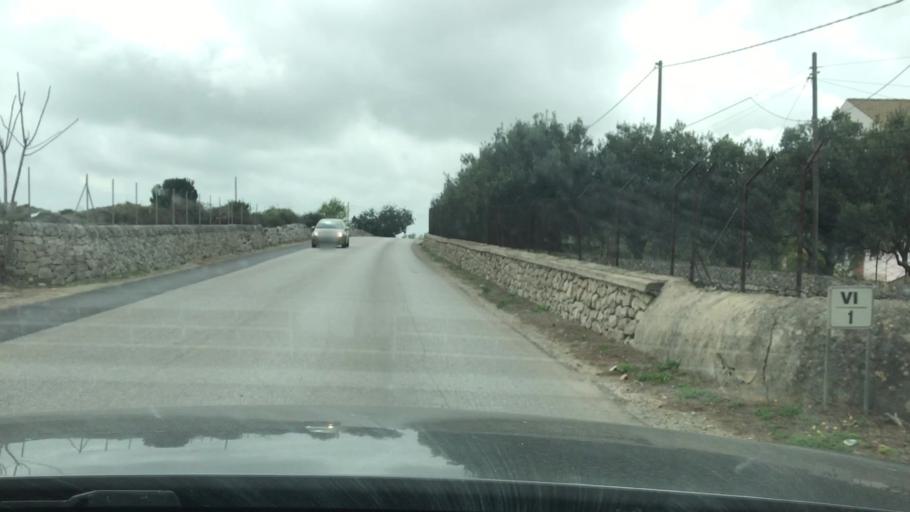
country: IT
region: Sicily
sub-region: Ragusa
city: Modica
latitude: 36.8231
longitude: 14.7488
